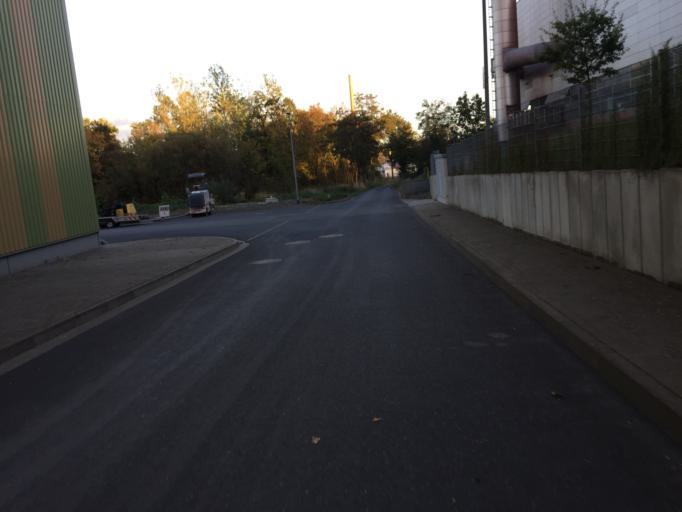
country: DE
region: Hesse
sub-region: Regierungsbezirk Giessen
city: Giessen
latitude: 50.5676
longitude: 8.6785
